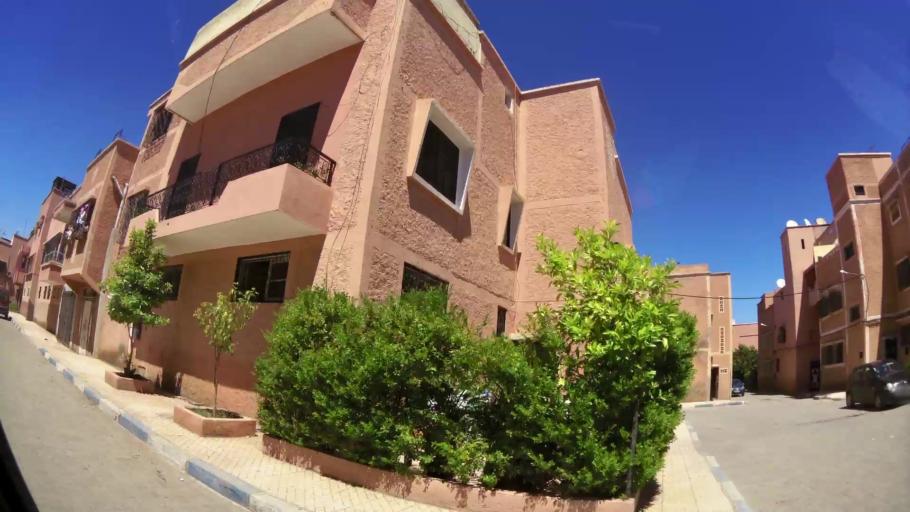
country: MA
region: Marrakech-Tensift-Al Haouz
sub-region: Marrakech
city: Marrakesh
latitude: 31.6505
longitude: -7.9902
